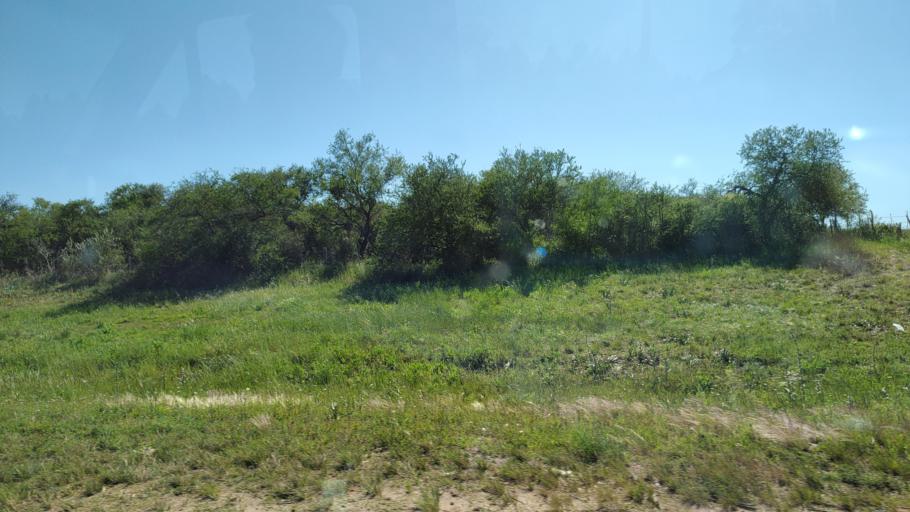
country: AR
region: Entre Rios
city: Ubajay
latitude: -31.9890
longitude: -58.3007
